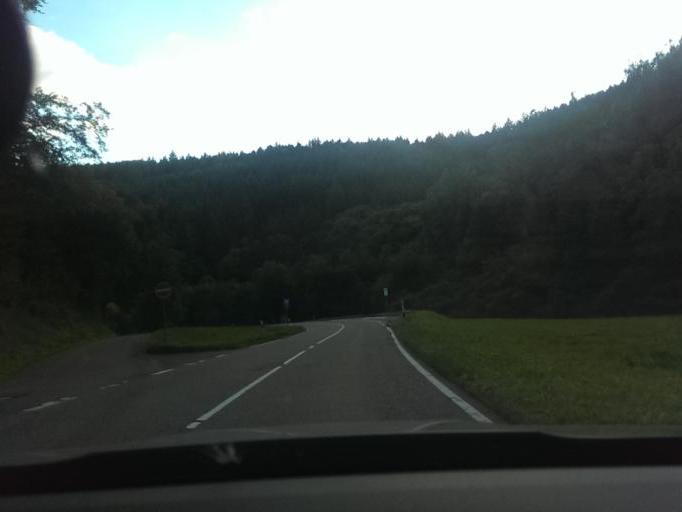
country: DE
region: Baden-Wuerttemberg
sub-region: Karlsruhe Region
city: Unterreichenbach
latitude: 48.8388
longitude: 8.7488
